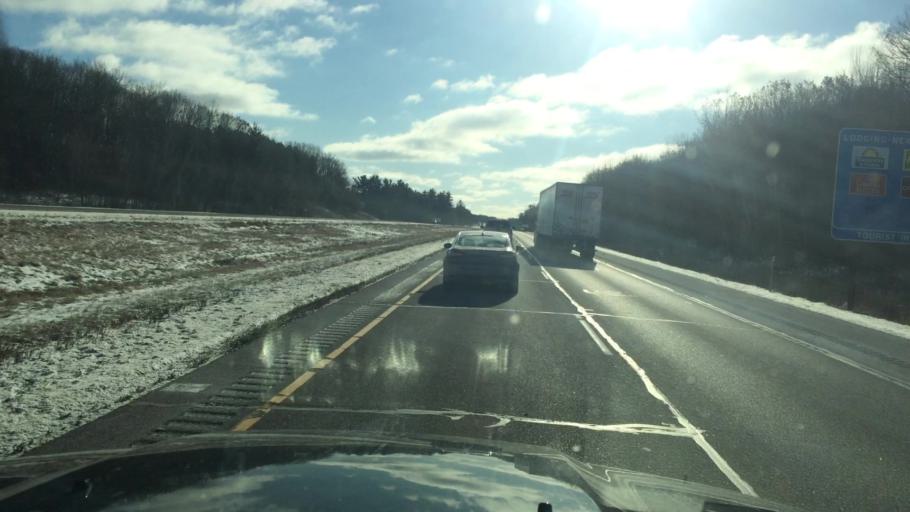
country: US
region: Wisconsin
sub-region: Portage County
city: Stevens Point
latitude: 44.5634
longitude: -89.5930
